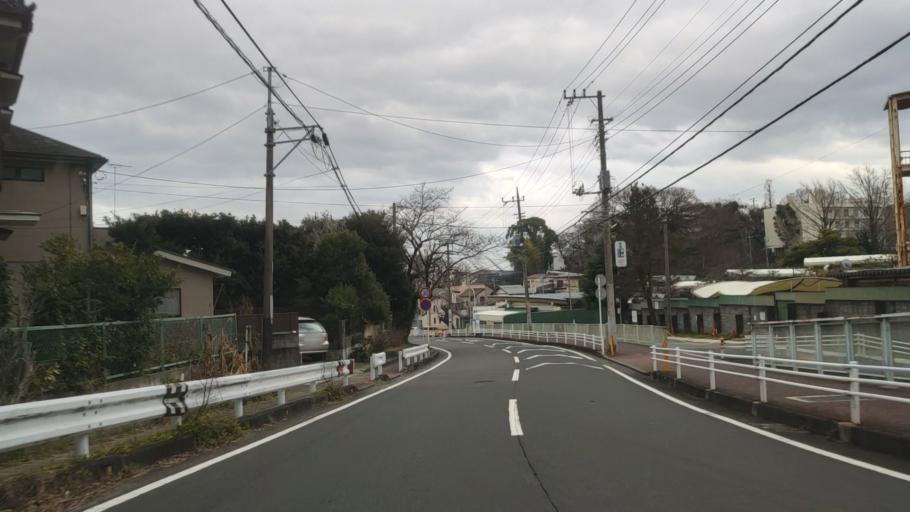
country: JP
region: Kanagawa
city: Odawara
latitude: 35.2519
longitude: 139.1497
